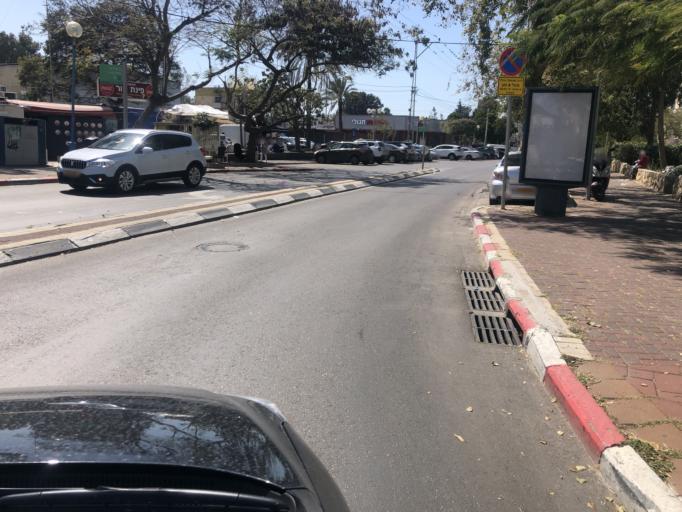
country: IL
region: Tel Aviv
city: Holon
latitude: 32.0061
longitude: 34.7645
